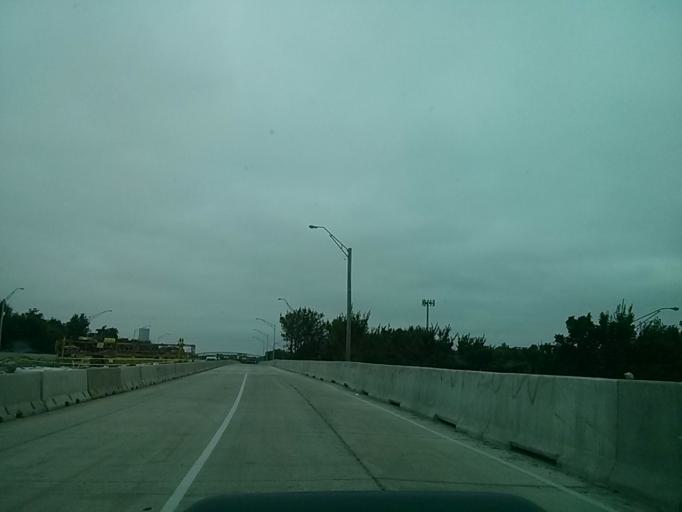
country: US
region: Oklahoma
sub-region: Tulsa County
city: Tulsa
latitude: 36.1604
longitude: -95.9483
